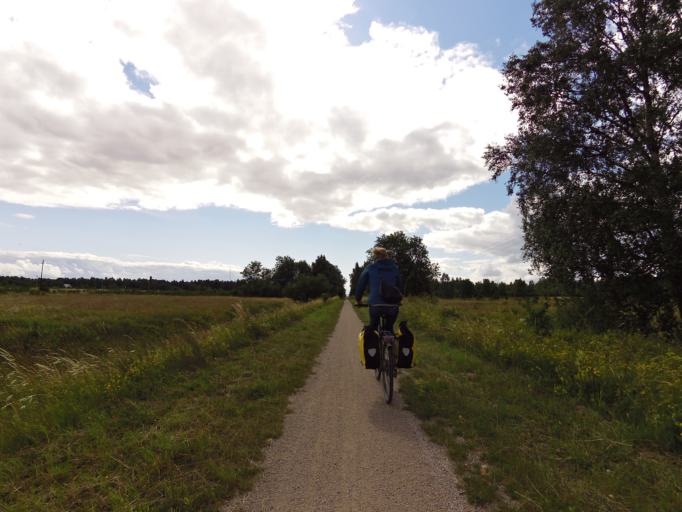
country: EE
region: Laeaene
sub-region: Haapsalu linn
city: Haapsalu
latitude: 58.9122
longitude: 23.4359
